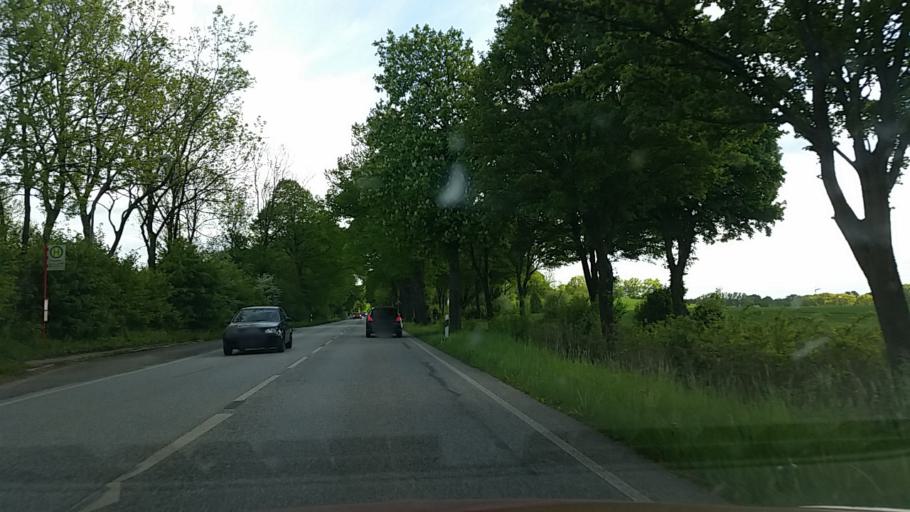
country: DE
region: Schleswig-Holstein
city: Delingsdorf
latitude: 53.6941
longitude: 10.2416
